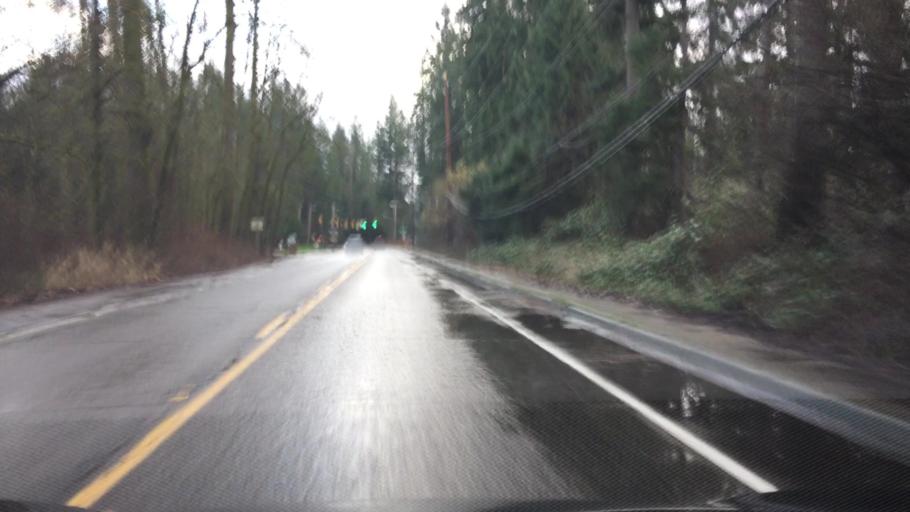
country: US
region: Washington
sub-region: King County
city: Cottage Lake
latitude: 47.7493
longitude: -122.0818
